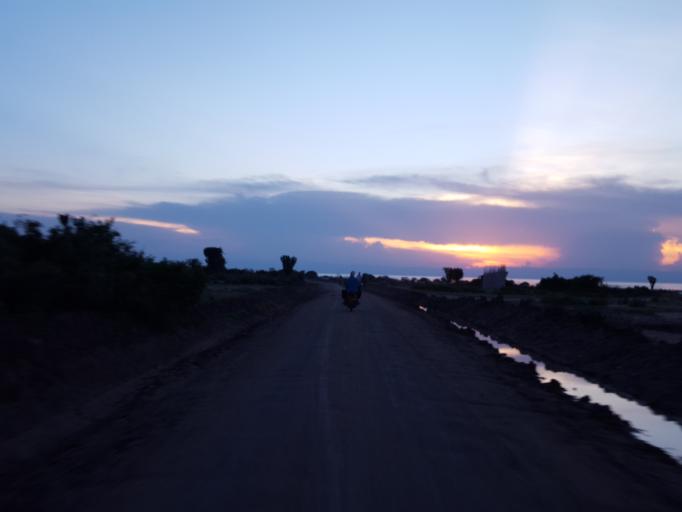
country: UG
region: Western Region
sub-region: Kibale District
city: Kagadi
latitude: 1.2377
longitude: 30.7431
